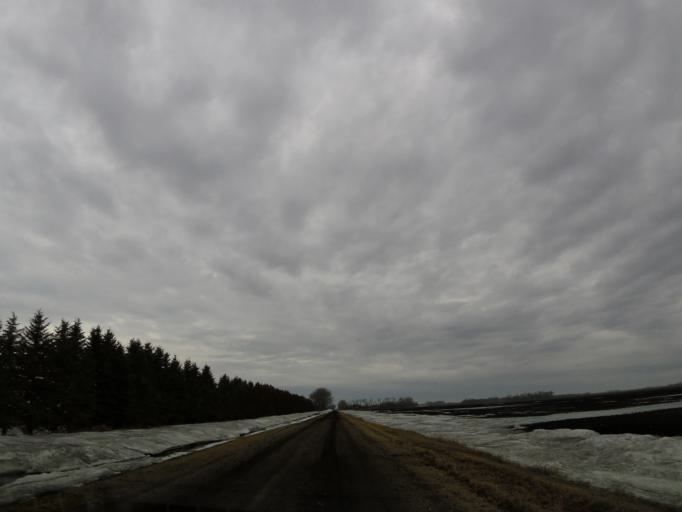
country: US
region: North Dakota
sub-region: Walsh County
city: Grafton
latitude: 48.3836
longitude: -97.4617
